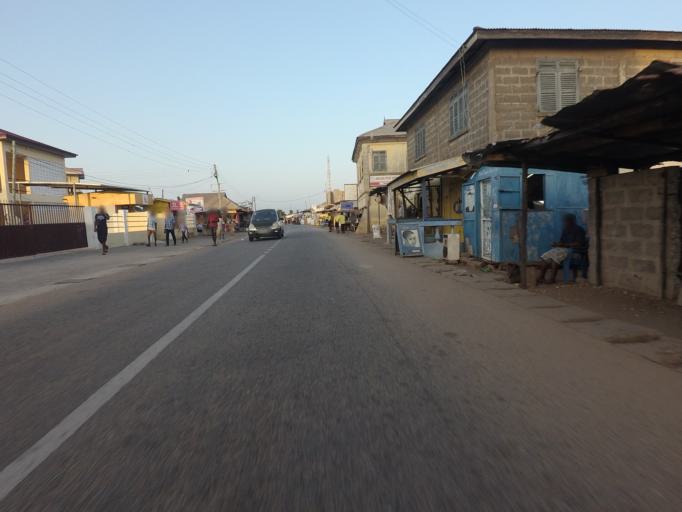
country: GH
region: Volta
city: Anloga
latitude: 5.7935
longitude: 0.8988
